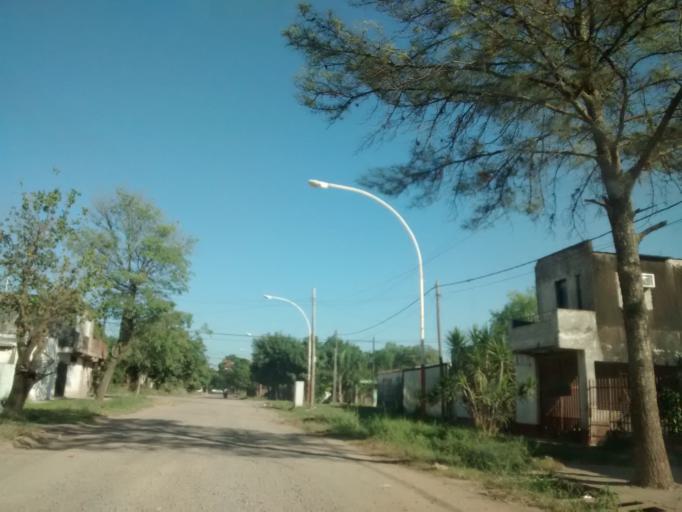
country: AR
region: Chaco
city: Resistencia
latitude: -27.4508
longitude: -58.9708
